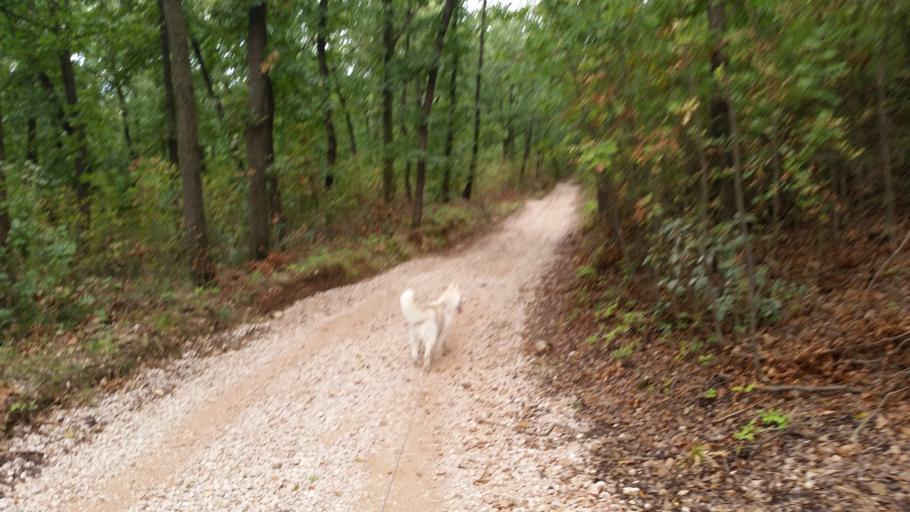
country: HU
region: Pest
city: Telki
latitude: 47.5666
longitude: 18.8272
